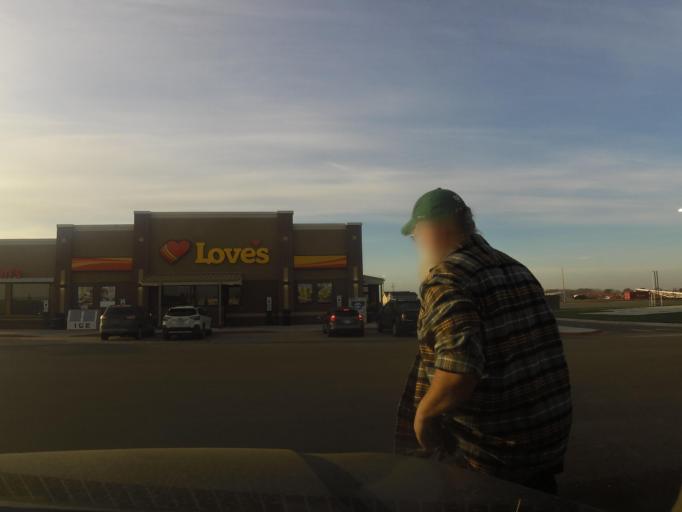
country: US
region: North Dakota
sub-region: Walsh County
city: Grafton
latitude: 48.5706
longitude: -97.1894
